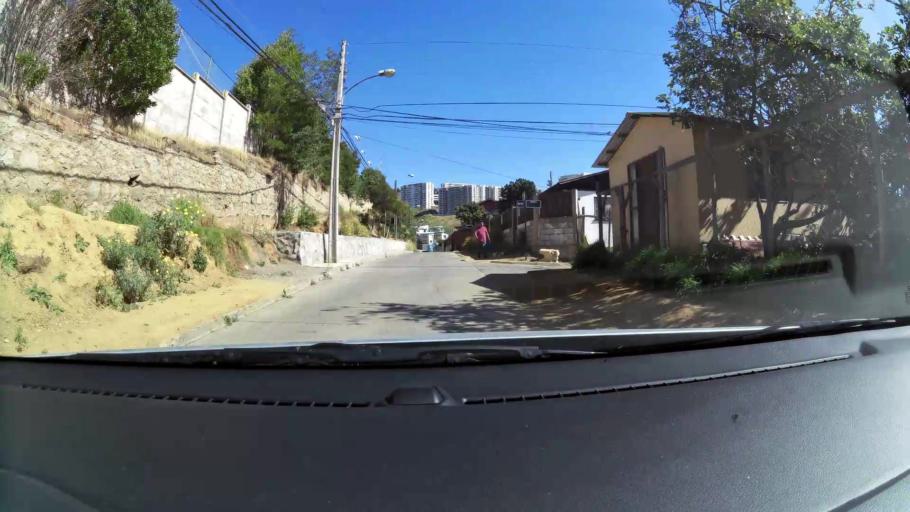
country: CL
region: Valparaiso
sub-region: Provincia de Valparaiso
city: Vina del Mar
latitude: -33.0322
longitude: -71.5727
